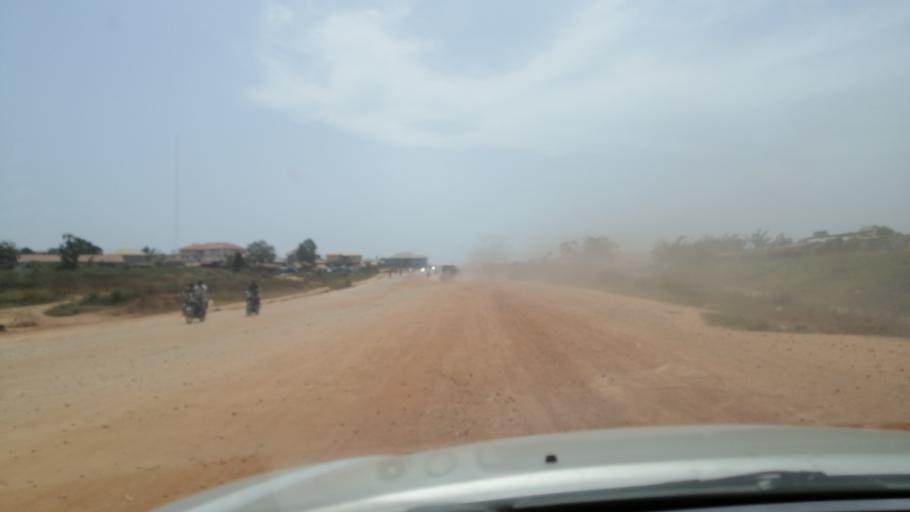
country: NG
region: Osun
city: Osogbo
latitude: 7.7878
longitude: 4.5784
